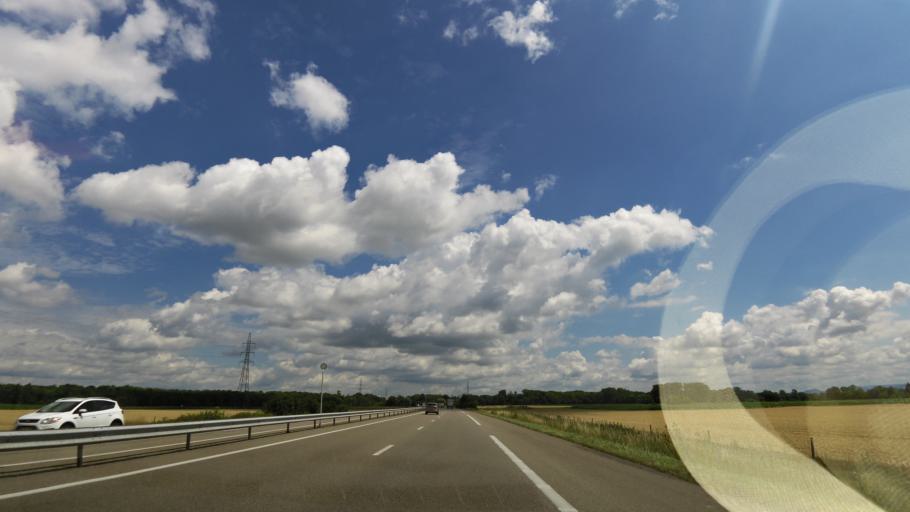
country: FR
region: Alsace
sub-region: Departement du Bas-Rhin
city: Drusenheim
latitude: 48.7756
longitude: 7.9470
